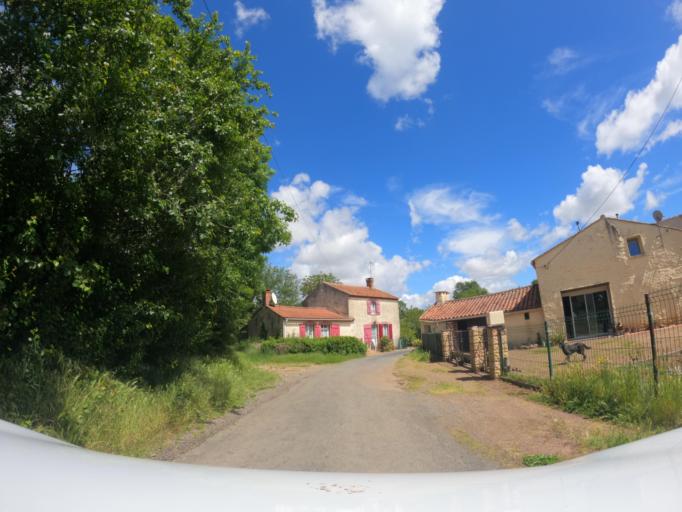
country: FR
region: Pays de la Loire
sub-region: Departement de la Vendee
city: Le Champ-Saint-Pere
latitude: 46.4933
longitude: -1.3350
